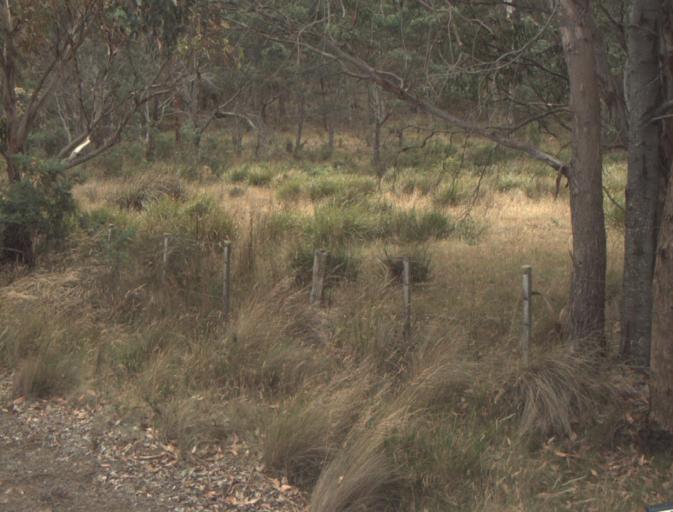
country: AU
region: Tasmania
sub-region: Northern Midlands
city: Evandale
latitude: -41.5245
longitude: 147.4603
